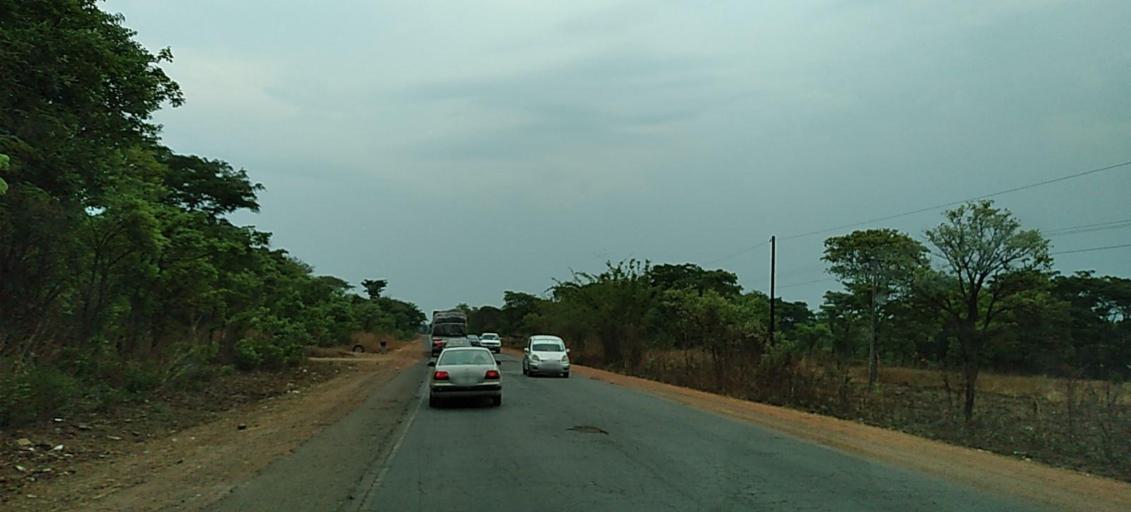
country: ZM
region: Copperbelt
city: Luanshya
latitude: -13.0866
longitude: 28.4376
